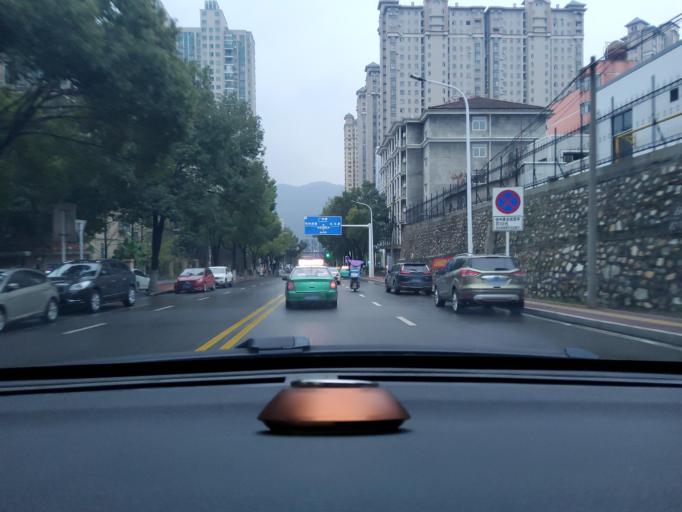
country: CN
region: Hubei
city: Tuanchengshan
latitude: 30.1907
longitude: 115.0275
